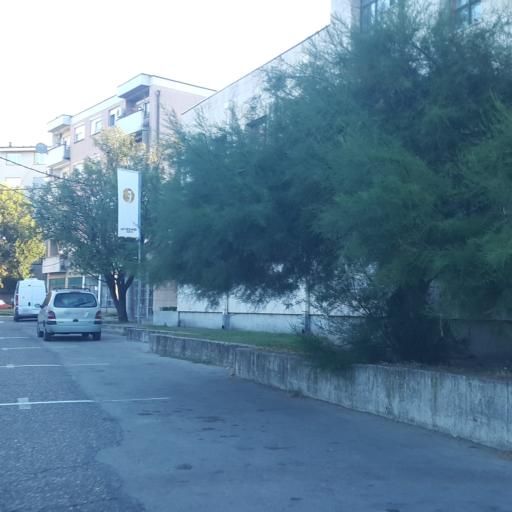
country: RS
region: Central Serbia
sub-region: Borski Okrug
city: Negotin
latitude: 44.2281
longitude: 22.5298
